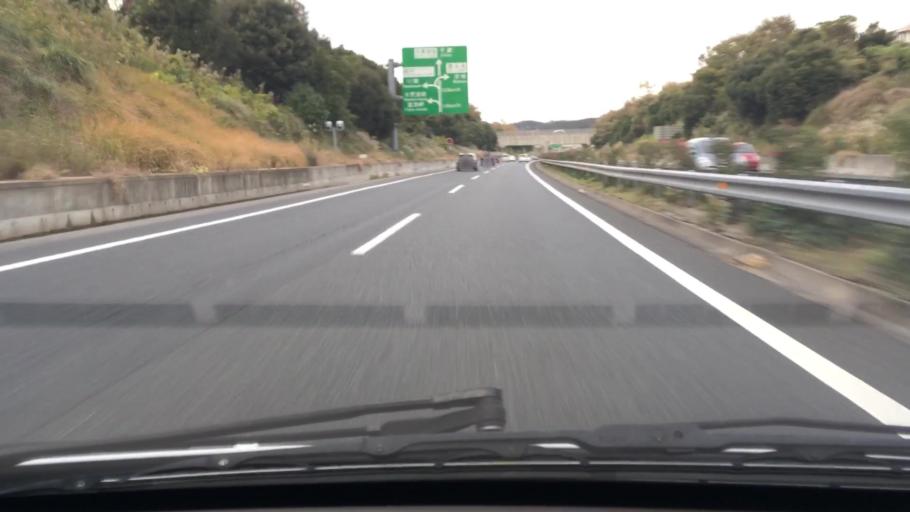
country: JP
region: Chiba
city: Kisarazu
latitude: 35.3380
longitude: 139.9445
